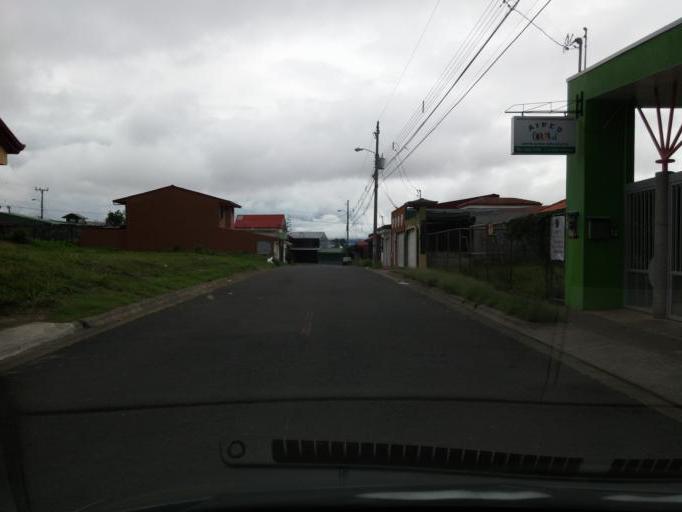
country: CR
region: Heredia
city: Mercedes
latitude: 10.0240
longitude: -84.1291
